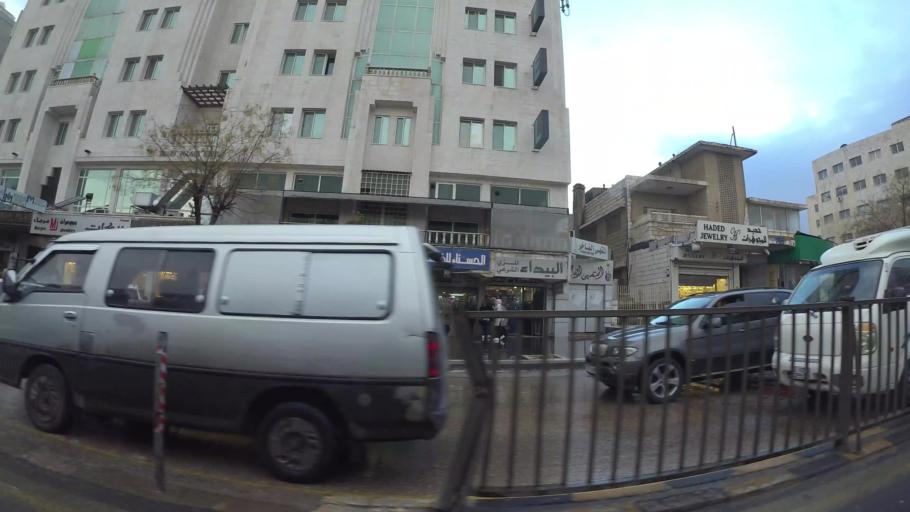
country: JO
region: Amman
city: Amman
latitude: 31.9689
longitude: 35.9159
